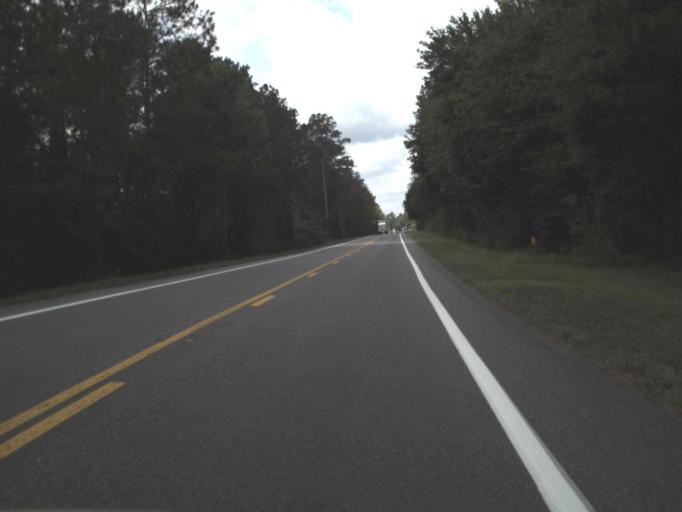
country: US
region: Florida
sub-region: Union County
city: Lake Butler
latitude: 30.0747
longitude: -82.2182
